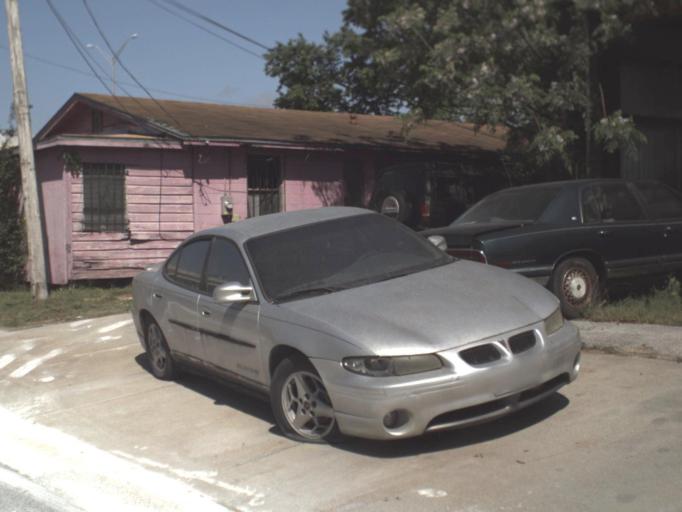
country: US
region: Florida
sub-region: Escambia County
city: Goulding
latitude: 30.4469
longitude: -87.2172
